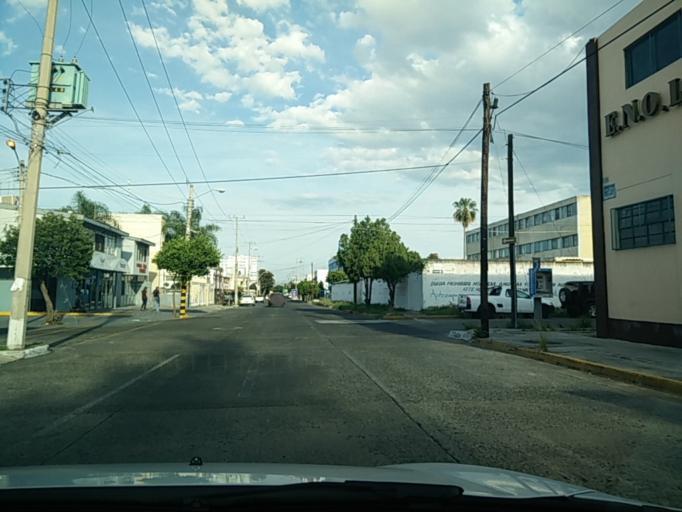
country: MX
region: Jalisco
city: Guadalajara
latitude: 20.6899
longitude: -103.3764
